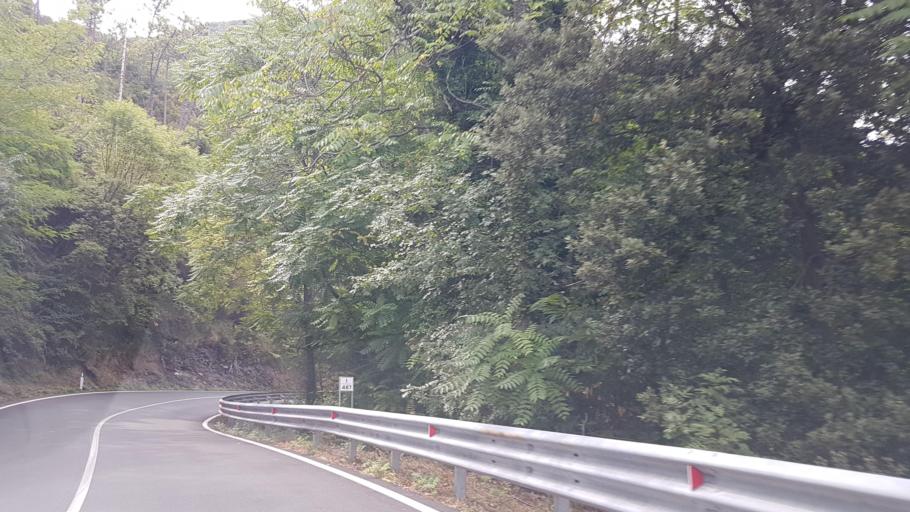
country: IT
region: Liguria
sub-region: Provincia di Genova
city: Casarza Ligure
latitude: 44.2590
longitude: 9.4624
